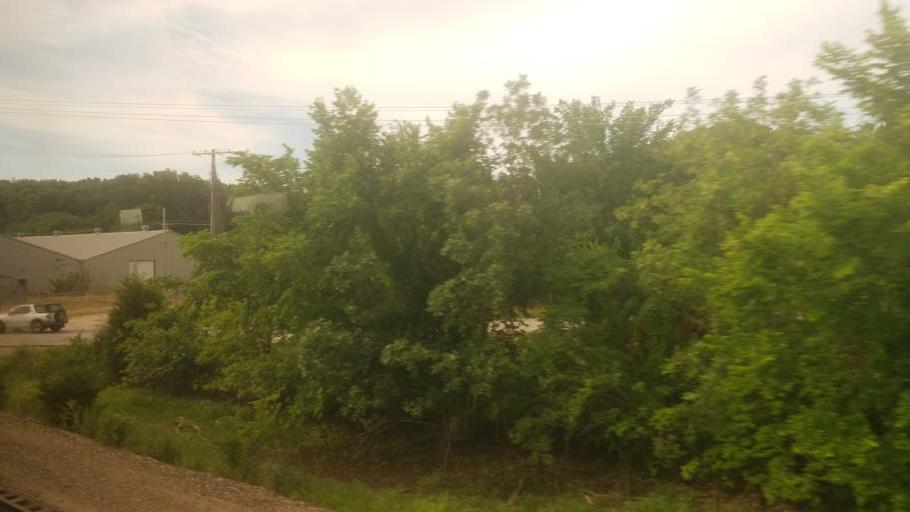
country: US
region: Kansas
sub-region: Douglas County
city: Lawrence
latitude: 38.9573
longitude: -95.2031
